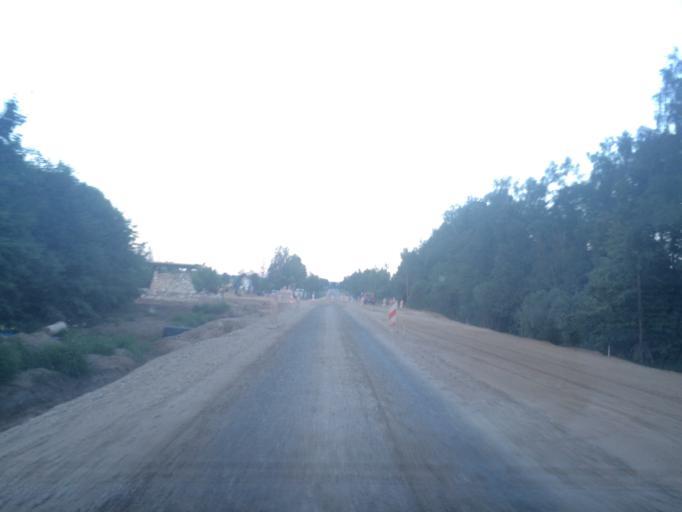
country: LT
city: Zarasai
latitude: 55.7524
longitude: 26.3210
